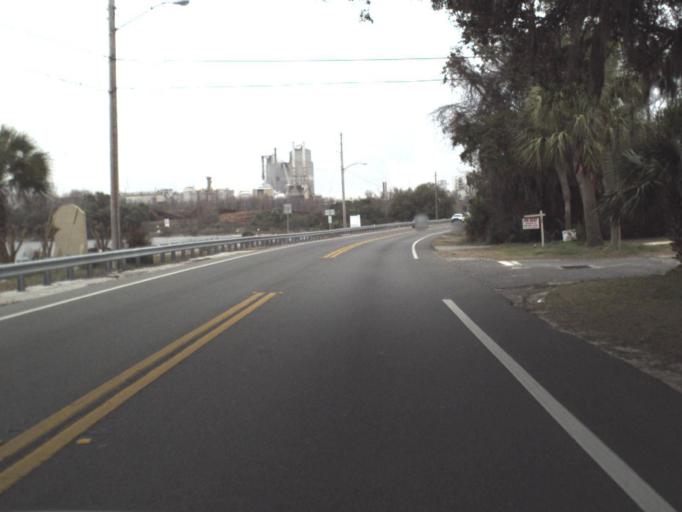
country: US
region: Florida
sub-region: Bay County
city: Parker
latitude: 30.1342
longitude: -85.6149
